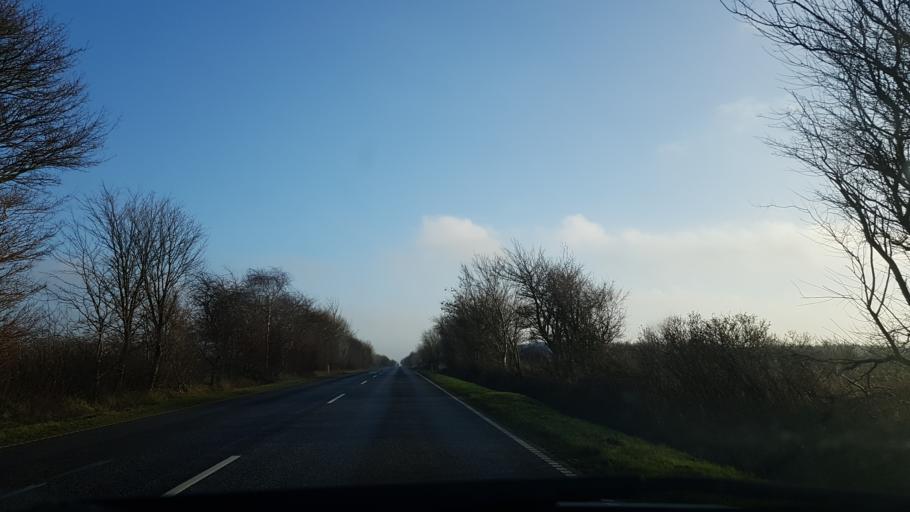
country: DK
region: South Denmark
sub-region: Haderslev Kommune
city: Vojens
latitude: 55.1847
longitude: 9.2263
